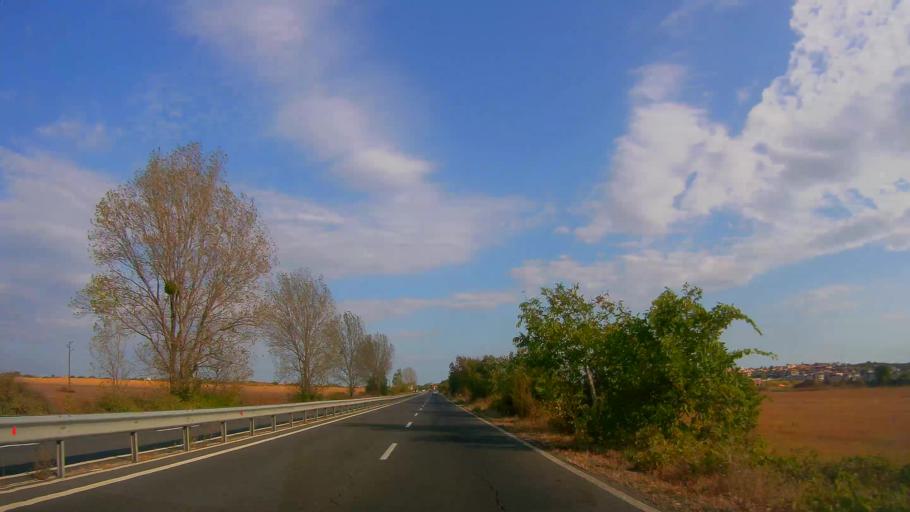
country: BG
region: Burgas
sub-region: Obshtina Sozopol
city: Chernomorets
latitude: 42.4250
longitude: 27.6412
